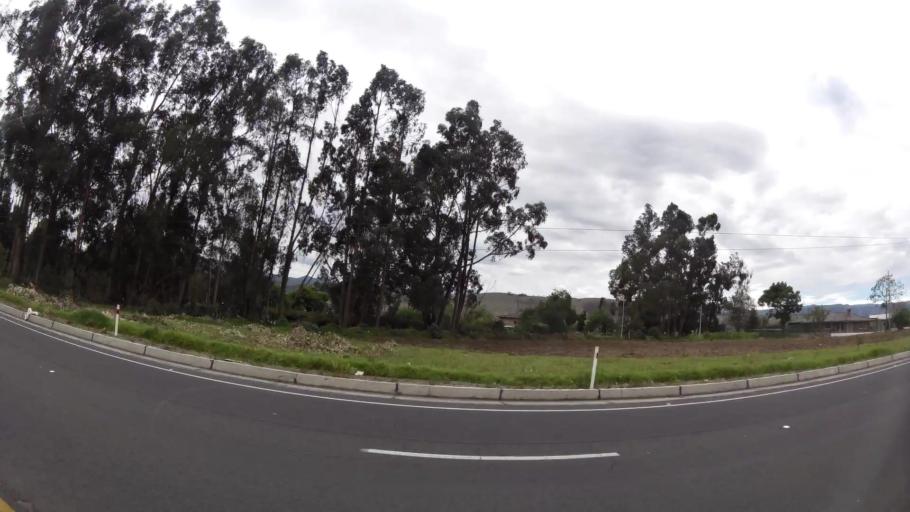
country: EC
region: Cotopaxi
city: San Miguel de Salcedo
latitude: -0.9960
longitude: -78.5948
